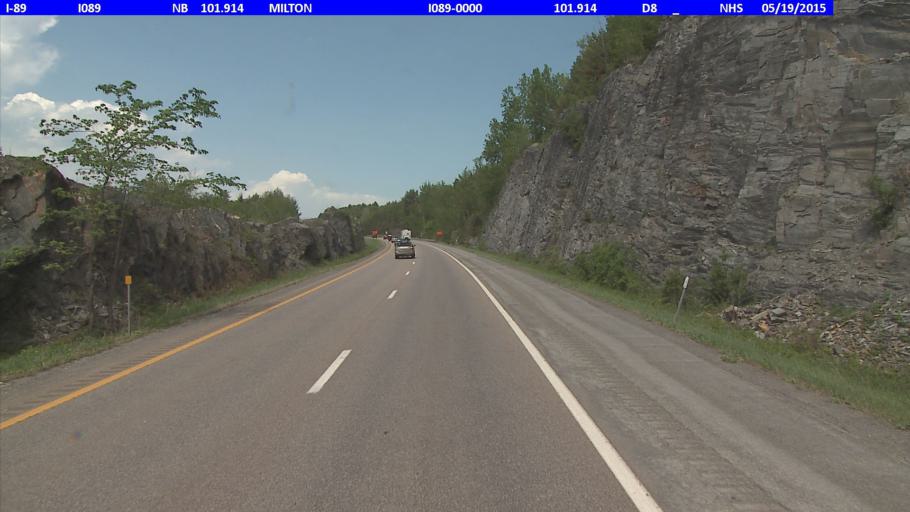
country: US
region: Vermont
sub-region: Chittenden County
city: Milton
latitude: 44.6409
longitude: -73.1395
